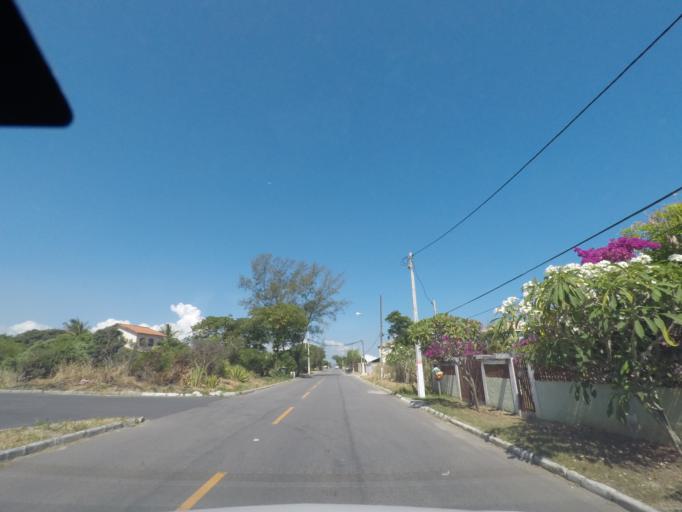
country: BR
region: Rio de Janeiro
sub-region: Marica
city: Marica
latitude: -22.9711
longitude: -42.9182
